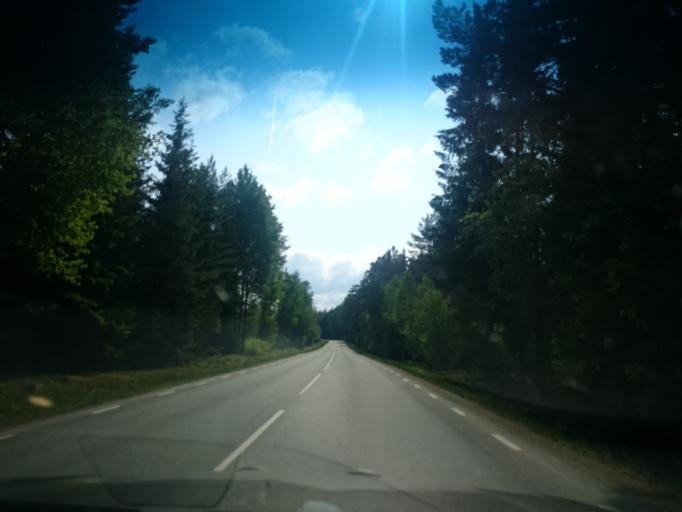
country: SE
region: Joenkoeping
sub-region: Vetlanda Kommun
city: Vetlanda
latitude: 57.4027
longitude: 14.9939
